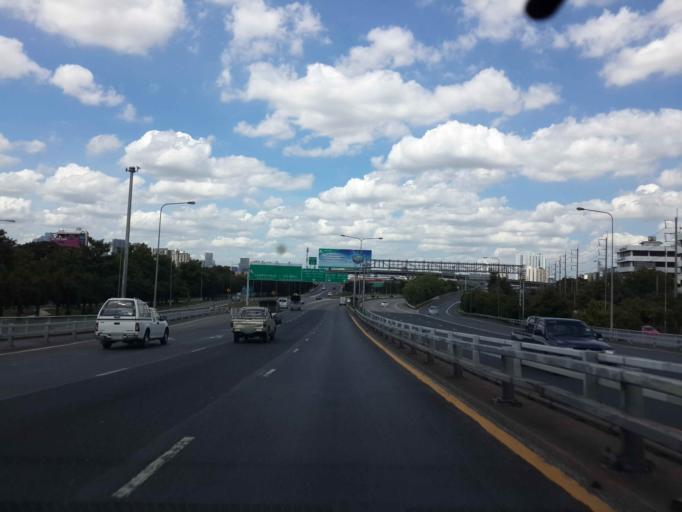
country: TH
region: Bangkok
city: Sathon
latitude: 13.6899
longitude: 100.5235
